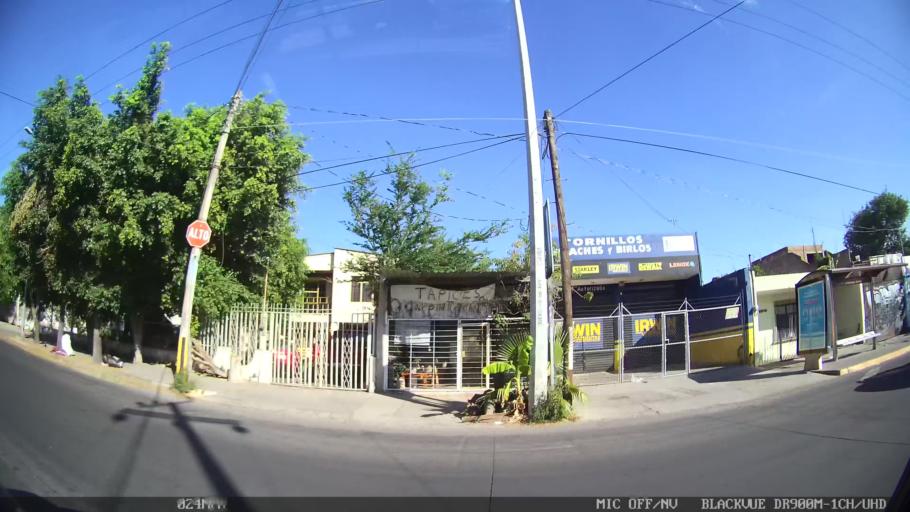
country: MX
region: Jalisco
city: Tlaquepaque
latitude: 20.7116
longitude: -103.3065
